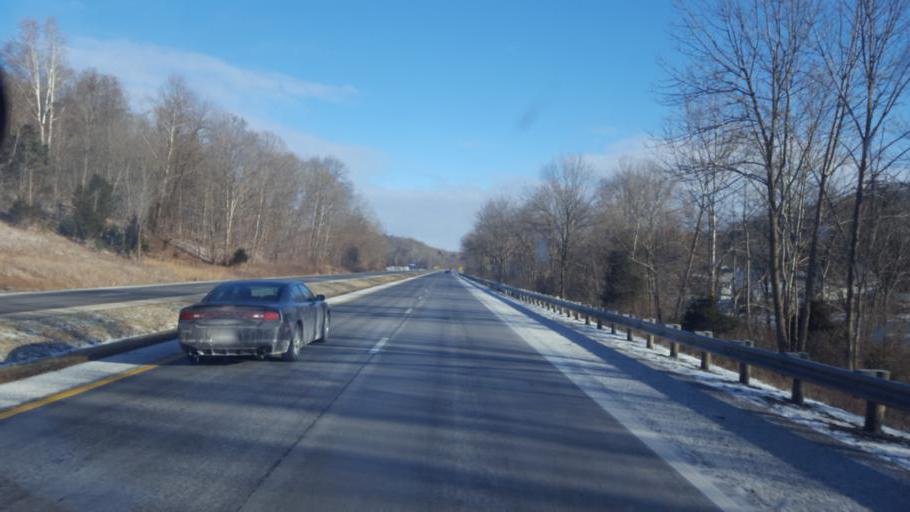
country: US
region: Ohio
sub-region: Ross County
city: Chillicothe
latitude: 39.2629
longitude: -82.9687
